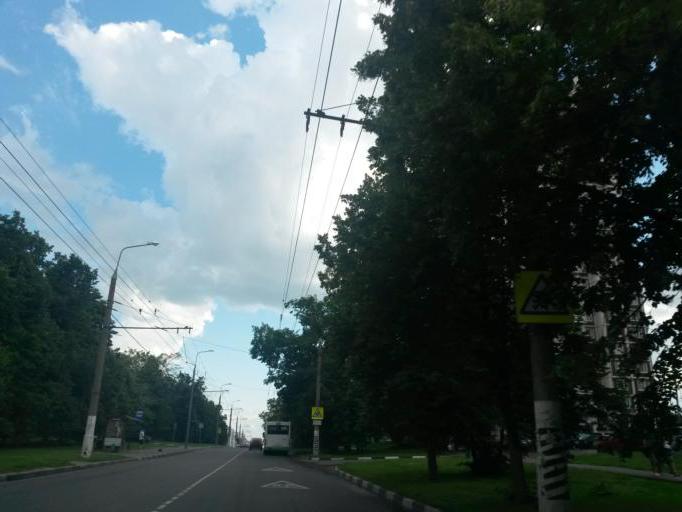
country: RU
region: Moscow
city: Orekhovo-Borisovo
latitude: 55.6183
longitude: 37.7436
